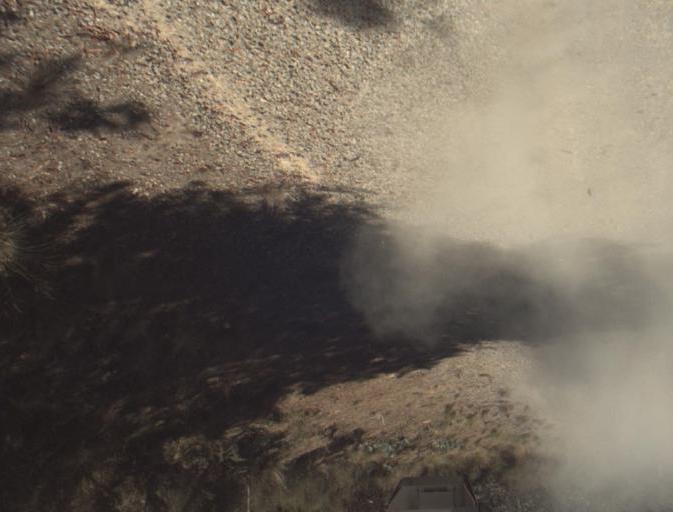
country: AU
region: Tasmania
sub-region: Dorset
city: Scottsdale
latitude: -41.3084
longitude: 147.4657
